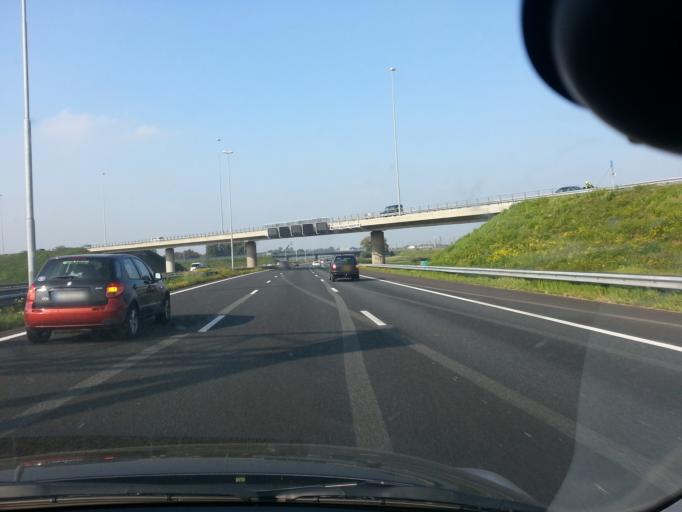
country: NL
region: North Brabant
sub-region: Gemeente Breda
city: Breda
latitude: 51.5800
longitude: 4.7253
